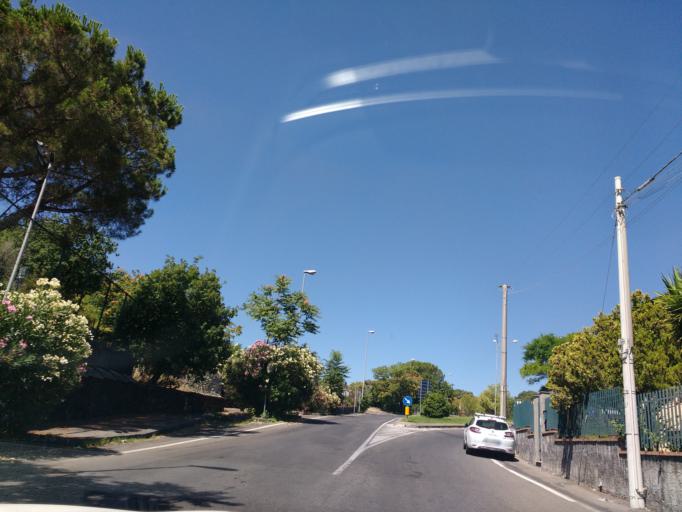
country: IT
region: Sicily
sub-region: Catania
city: Nicolosi
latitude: 37.6088
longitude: 15.0193
